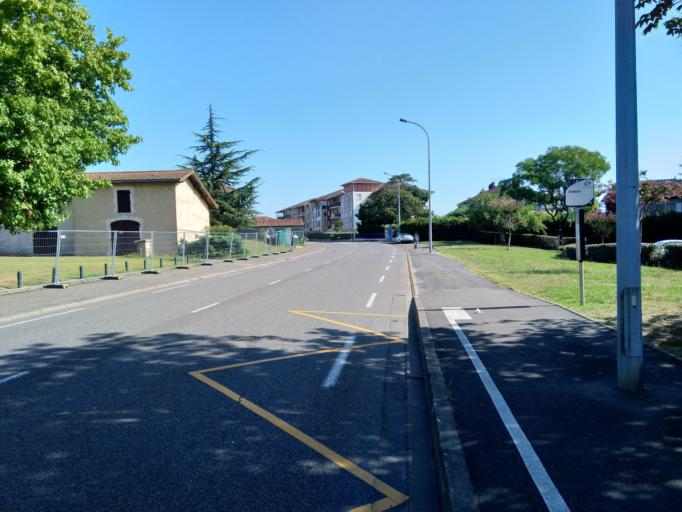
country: FR
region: Aquitaine
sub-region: Departement des Landes
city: Saint-Paul-les-Dax
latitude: 43.7268
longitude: -1.0497
